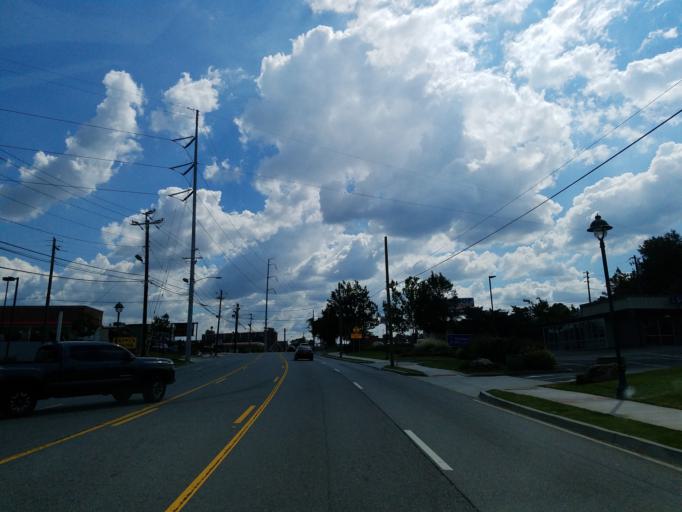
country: US
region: Georgia
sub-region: Fulton County
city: Sandy Springs
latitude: 33.9315
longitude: -84.3800
